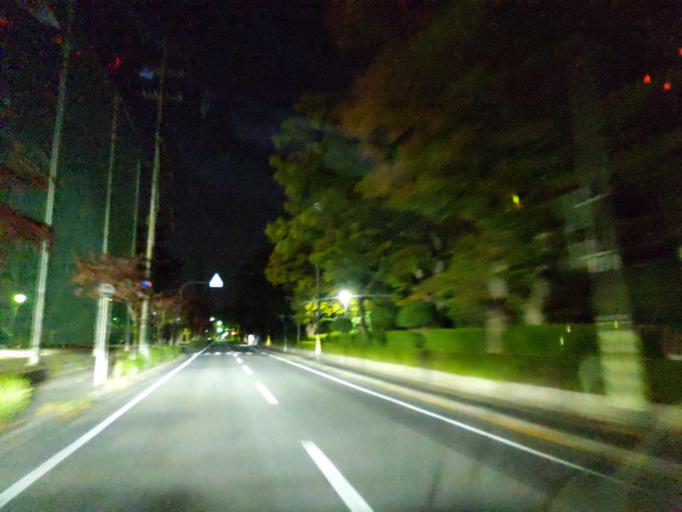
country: JP
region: Okayama
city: Okayama-shi
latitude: 34.6877
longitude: 133.9233
